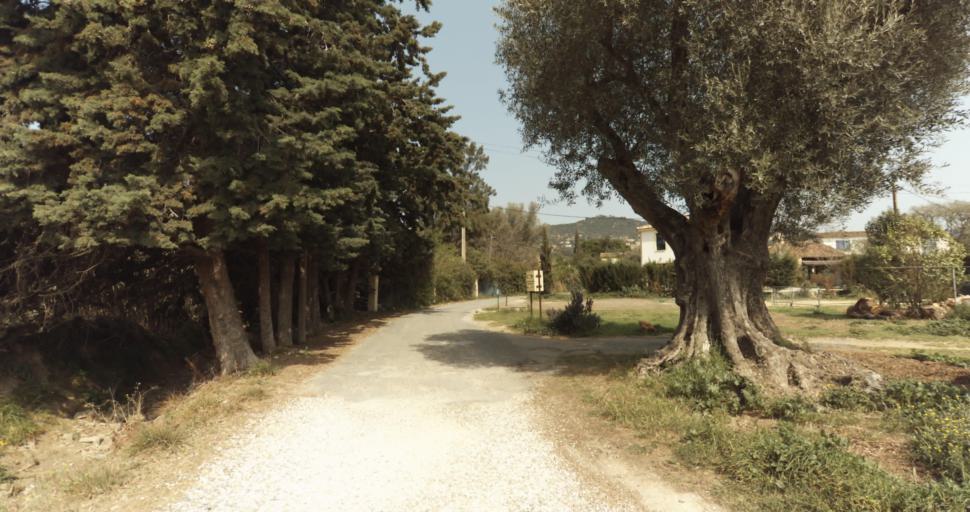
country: FR
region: Provence-Alpes-Cote d'Azur
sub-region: Departement du Var
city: Bormes-les-Mimosas
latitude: 43.1398
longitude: 6.3364
